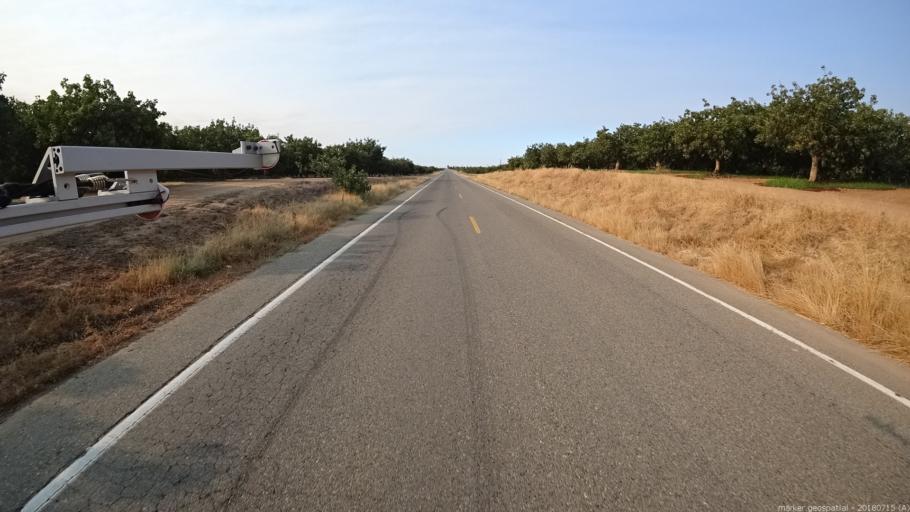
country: US
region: California
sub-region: Madera County
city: Madera Acres
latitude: 37.0432
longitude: -120.0564
